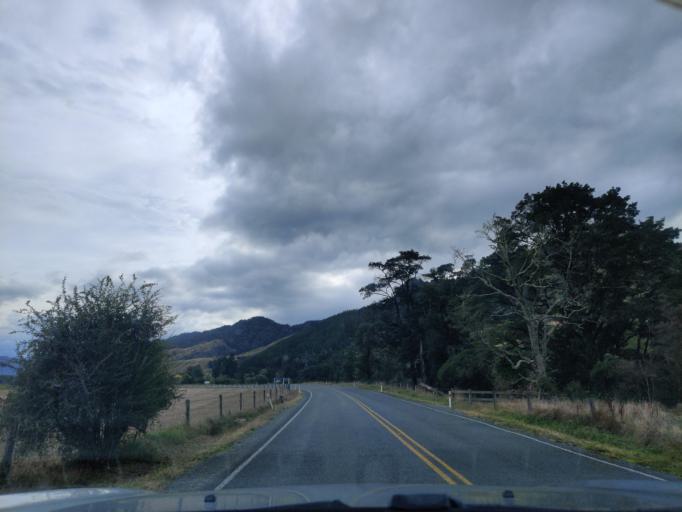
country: NZ
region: Tasman
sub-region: Tasman District
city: Wakefield
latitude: -41.7584
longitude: 172.3888
